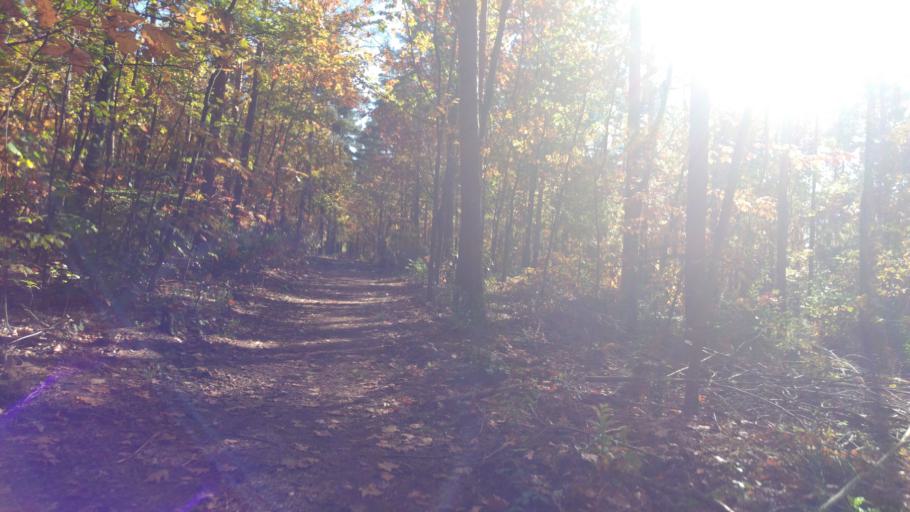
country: DE
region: Saxony
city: Albertstadt
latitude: 51.1044
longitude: 13.7662
